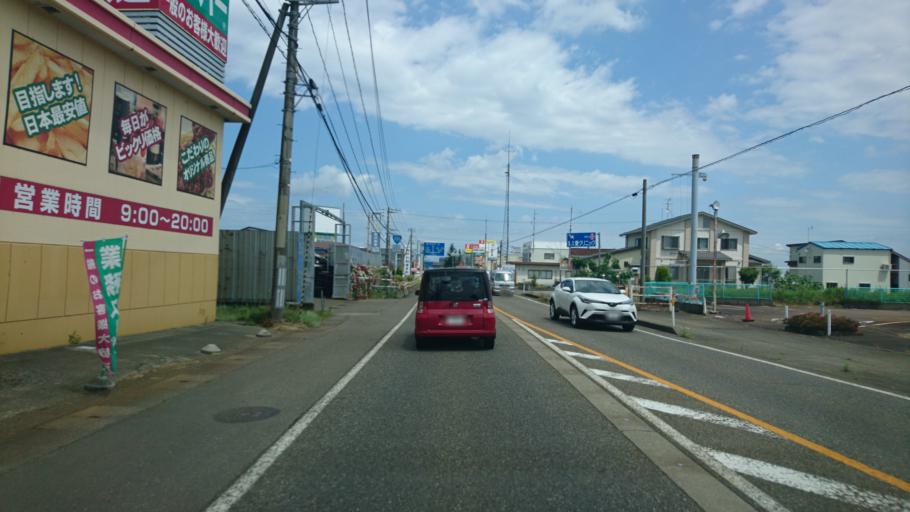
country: JP
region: Niigata
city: Arai
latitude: 37.0563
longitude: 138.2603
